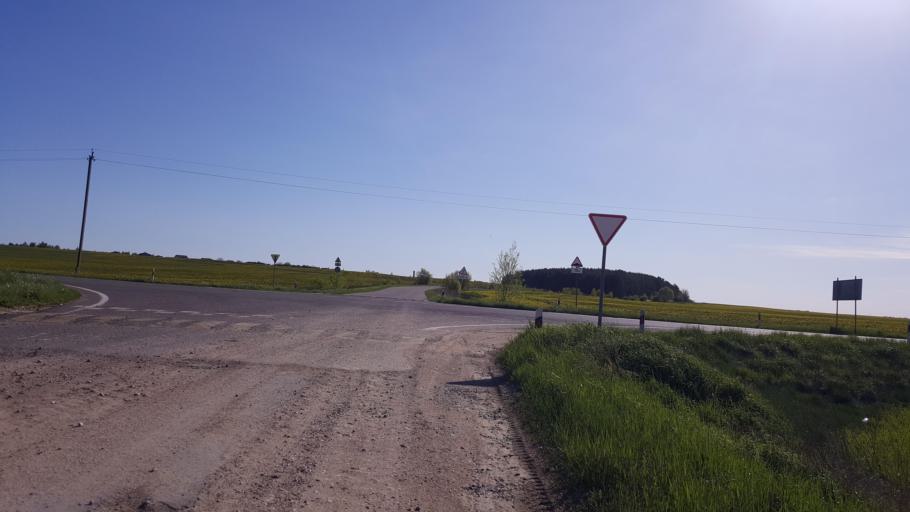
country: BY
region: Brest
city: Kamyanyets
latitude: 52.4116
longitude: 23.8537
